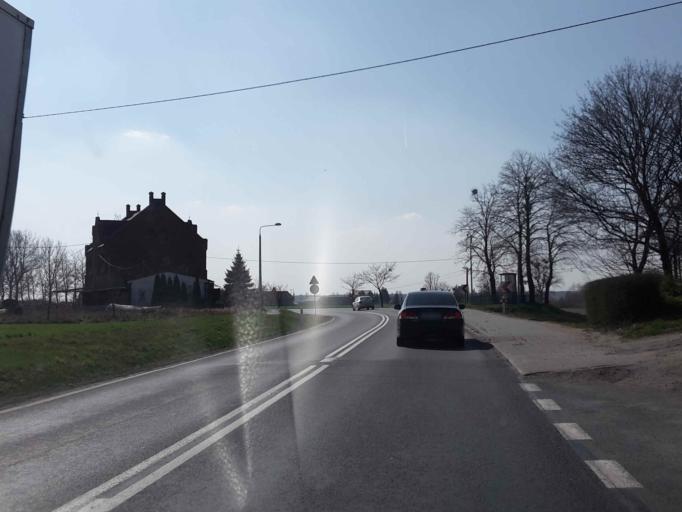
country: PL
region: Kujawsko-Pomorskie
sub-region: Powiat golubsko-dobrzynski
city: Kowalewo Pomorskie
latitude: 53.1333
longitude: 18.8488
